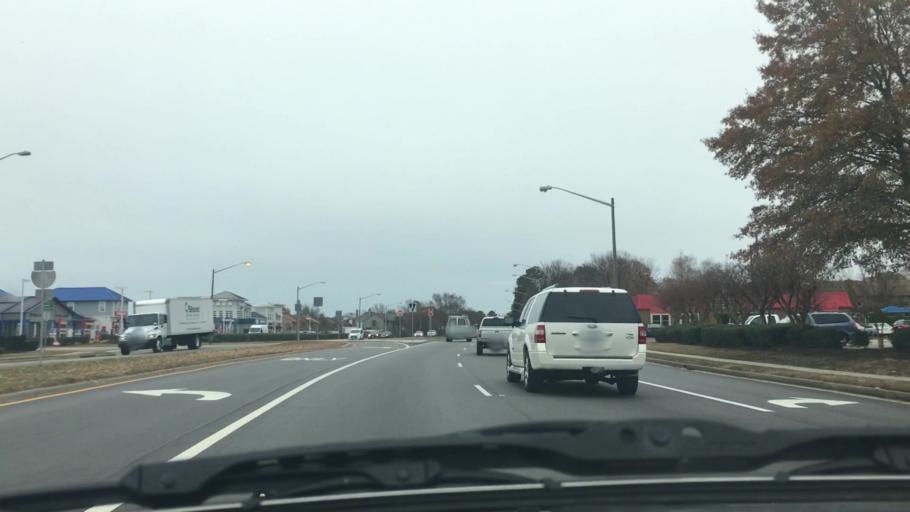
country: US
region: Virginia
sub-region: City of Chesapeake
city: Chesapeake
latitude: 36.8225
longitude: -76.1270
